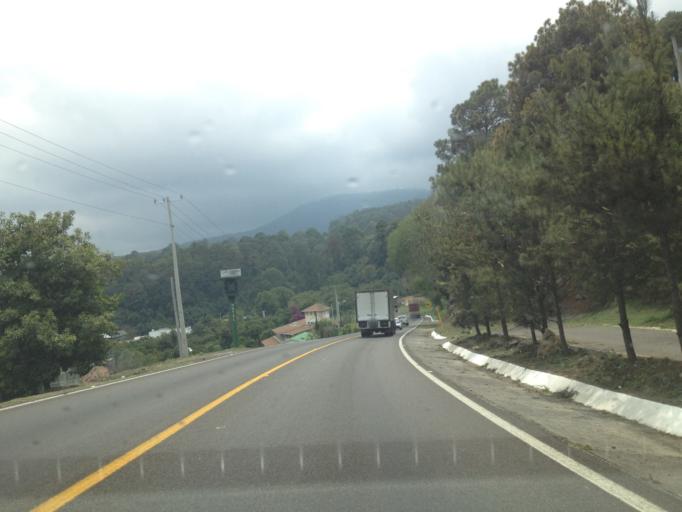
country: MX
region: Michoacan
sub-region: Uruapan
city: Toreo Bajo (El Toreo Bajo)
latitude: 19.4533
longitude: -102.0024
